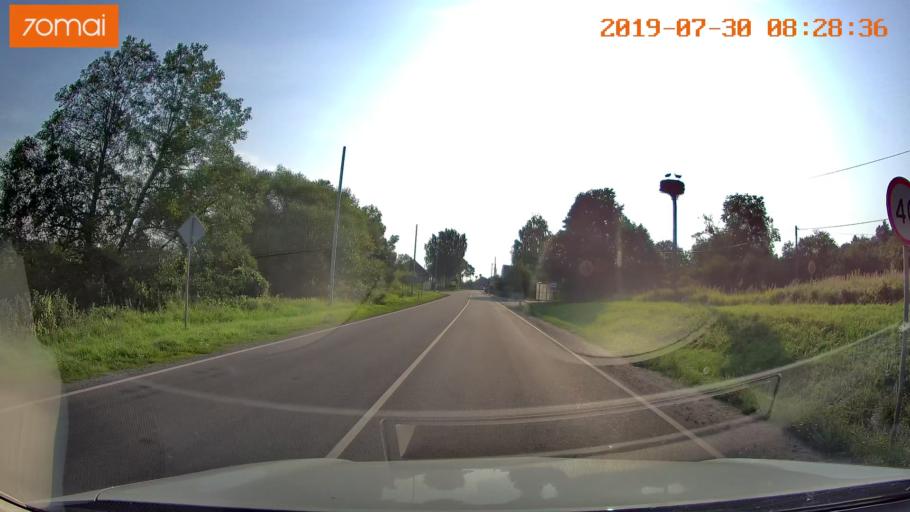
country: RU
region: Kaliningrad
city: Chernyakhovsk
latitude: 54.6298
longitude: 21.6483
